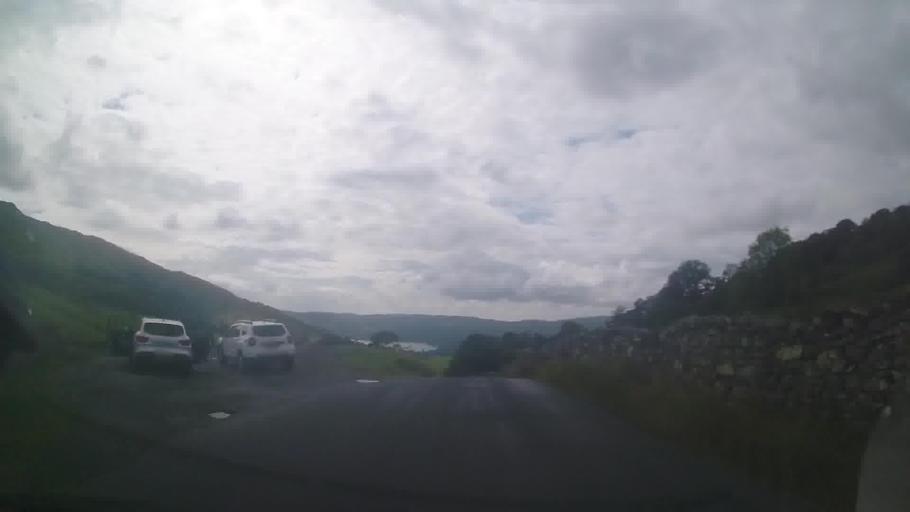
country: GB
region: England
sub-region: Cumbria
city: Ambleside
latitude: 54.4431
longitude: -2.9442
